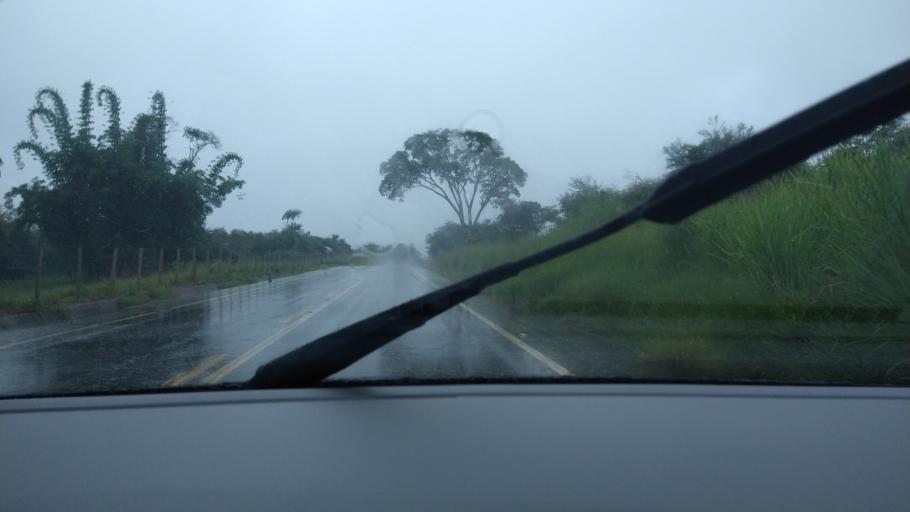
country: BR
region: Minas Gerais
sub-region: Ponte Nova
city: Ponte Nova
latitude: -20.5454
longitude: -42.8865
